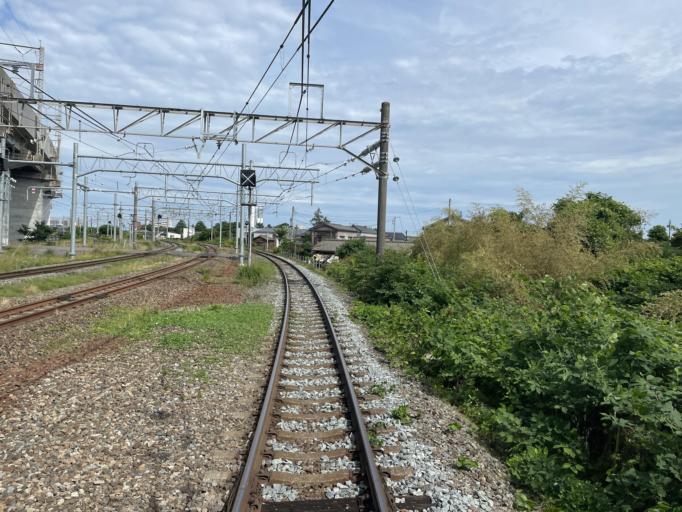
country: JP
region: Niigata
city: Kameda-honcho
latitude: 37.9140
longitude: 139.0774
